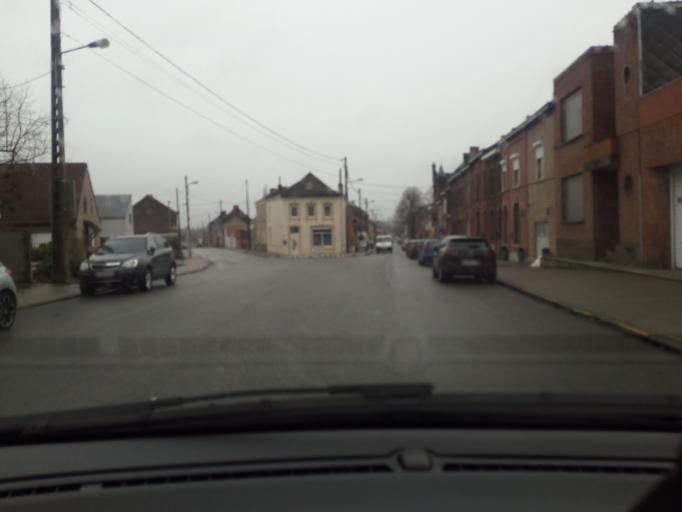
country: BE
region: Wallonia
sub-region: Province du Hainaut
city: Colfontaine
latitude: 50.4224
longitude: 3.8640
